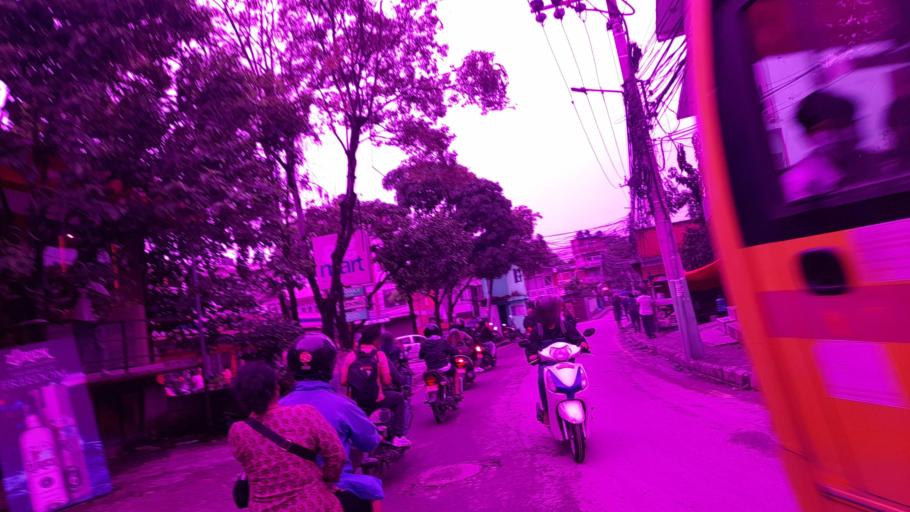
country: NP
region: Central Region
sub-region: Bagmati Zone
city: Kathmandu
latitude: 27.7008
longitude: 85.2962
